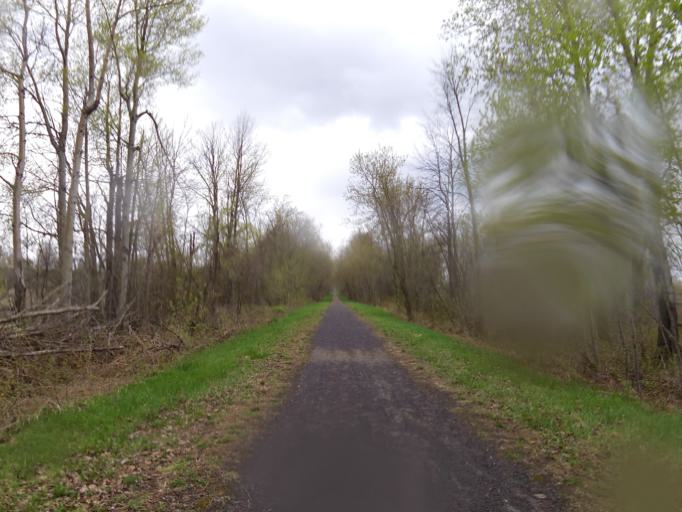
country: CA
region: Ontario
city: Bourget
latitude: 45.4347
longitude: -75.2446
